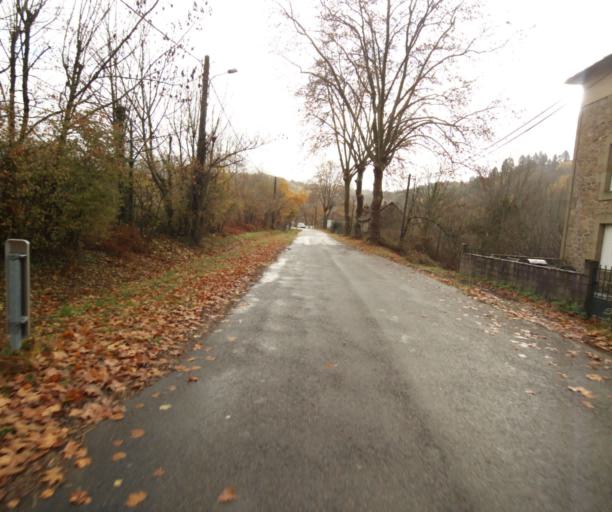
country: FR
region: Limousin
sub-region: Departement de la Correze
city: Cornil
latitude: 45.1803
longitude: 1.6482
